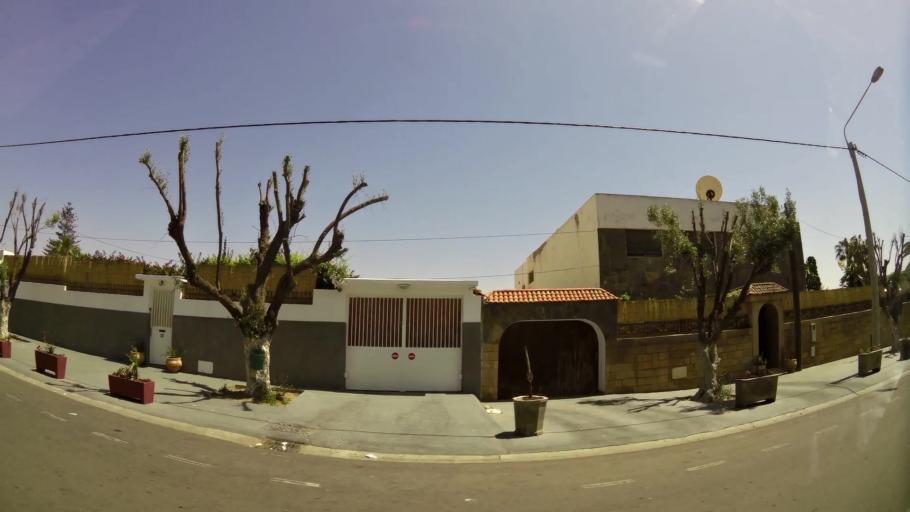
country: MA
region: Souss-Massa-Draa
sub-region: Agadir-Ida-ou-Tnan
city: Agadir
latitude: 30.4246
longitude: -9.6037
